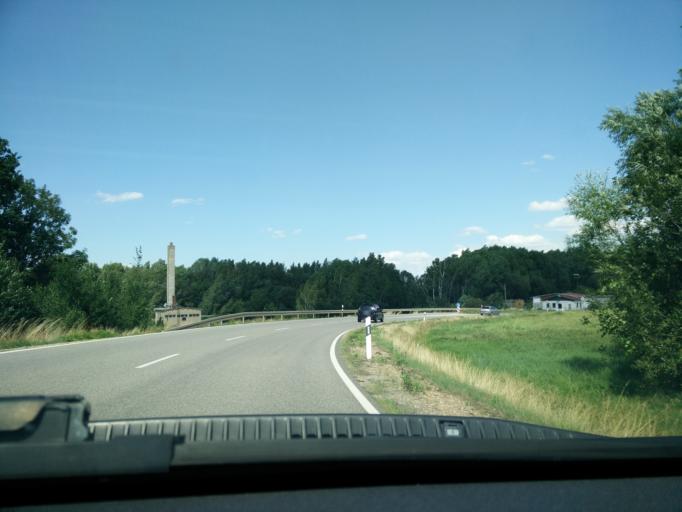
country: DE
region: Saxony
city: Penig
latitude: 50.9499
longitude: 12.6801
